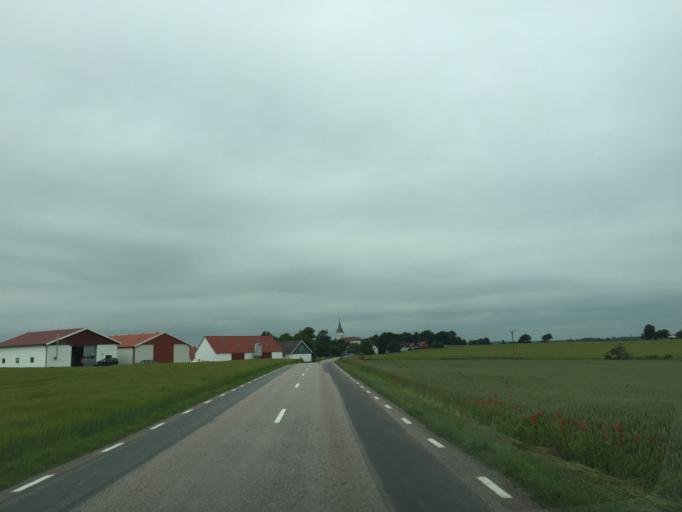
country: SE
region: Skane
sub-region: Ystads Kommun
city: Kopingebro
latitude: 55.4324
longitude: 14.0459
